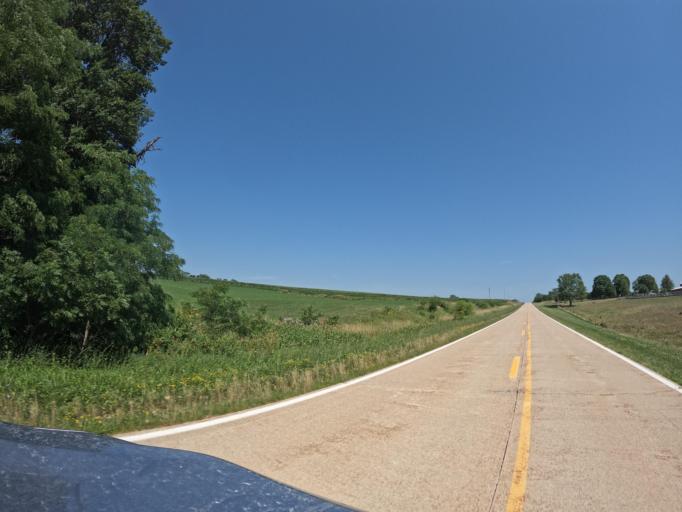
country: US
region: Iowa
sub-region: Henry County
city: Mount Pleasant
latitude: 40.8754
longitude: -91.5602
